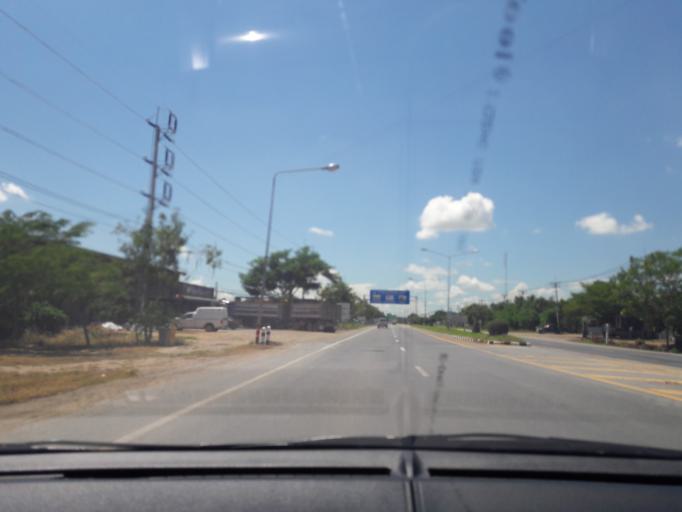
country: TH
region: Kanchanaburi
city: Tha Maka
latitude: 14.0356
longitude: 99.8083
